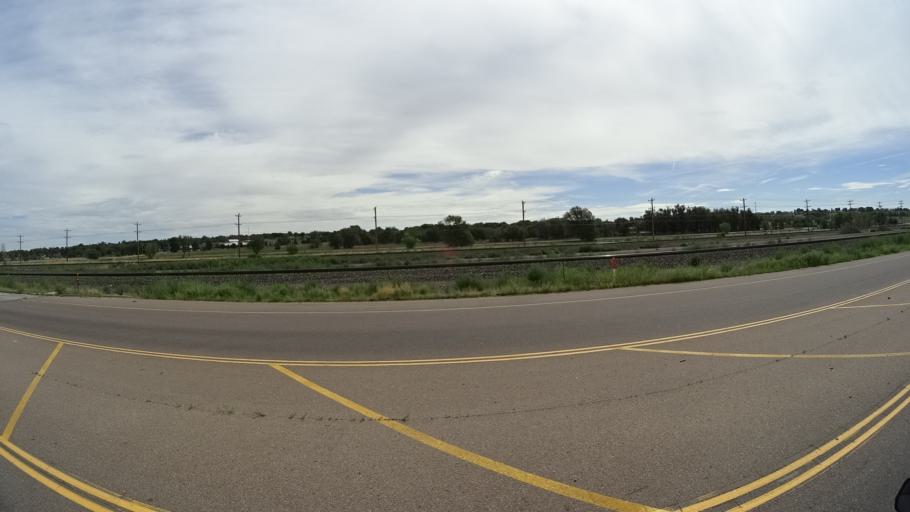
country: US
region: Colorado
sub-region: El Paso County
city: Security-Widefield
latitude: 38.7169
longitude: -104.7155
